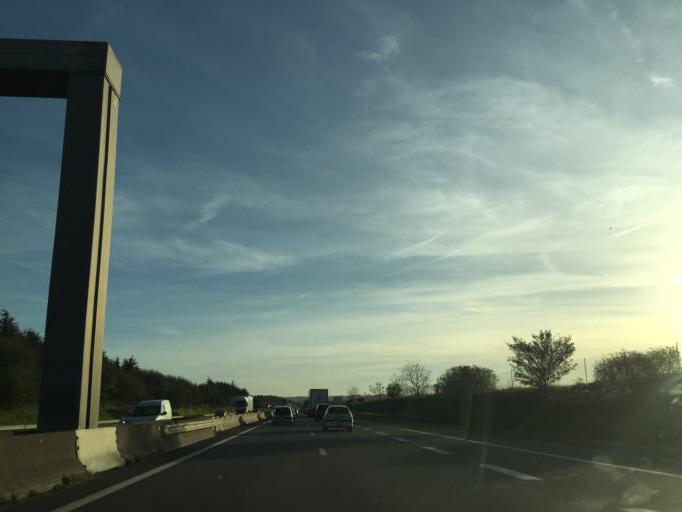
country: FR
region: Rhone-Alpes
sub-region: Departement du Rhone
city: Corbas
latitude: 45.6589
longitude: 4.9221
